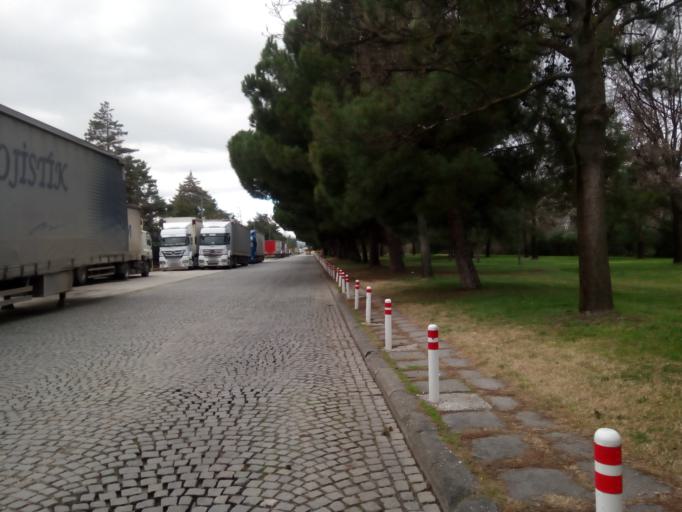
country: TR
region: Bursa
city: Niluefer
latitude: 40.2461
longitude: 28.9624
